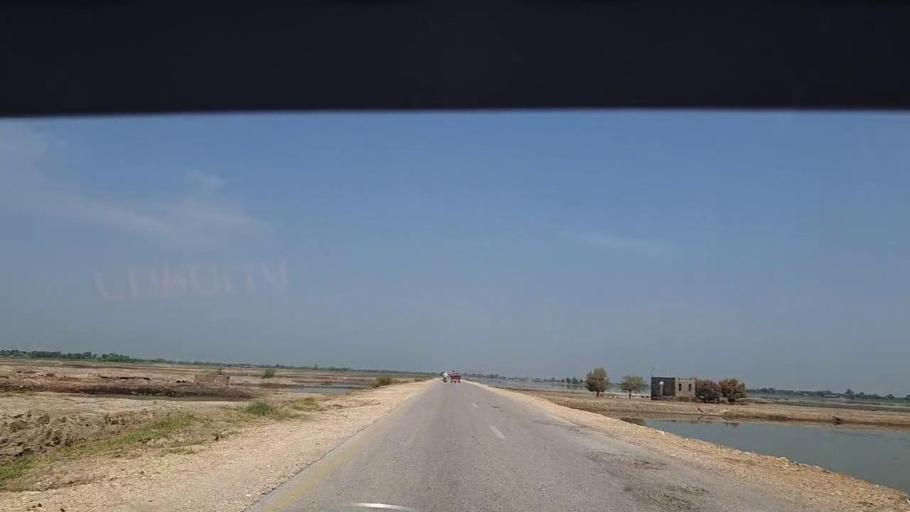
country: PK
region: Sindh
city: Rustam jo Goth
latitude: 28.0871
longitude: 68.7981
